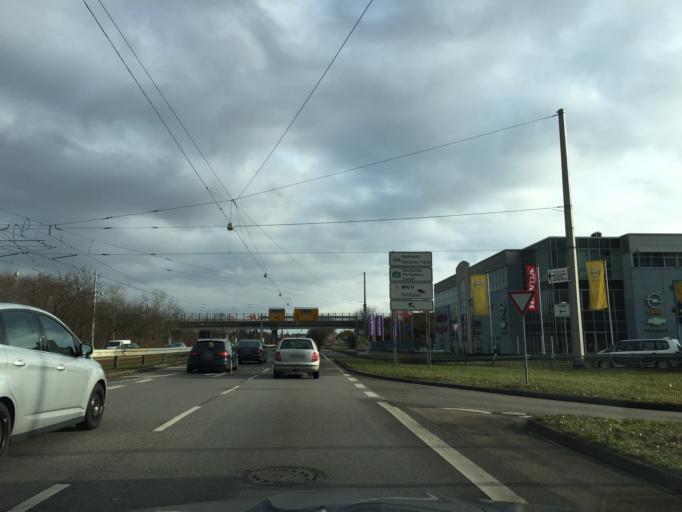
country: DE
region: Rheinland-Pfalz
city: Altrip
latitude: 49.4458
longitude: 8.5096
